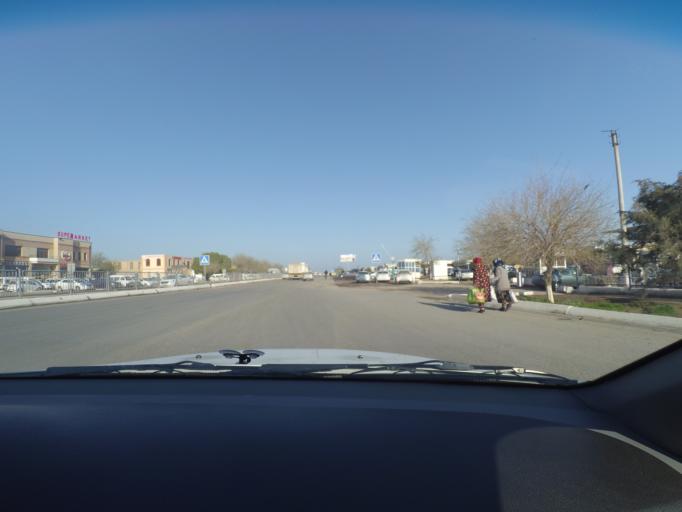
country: UZ
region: Bukhara
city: Bukhara
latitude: 39.8040
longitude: 64.4267
